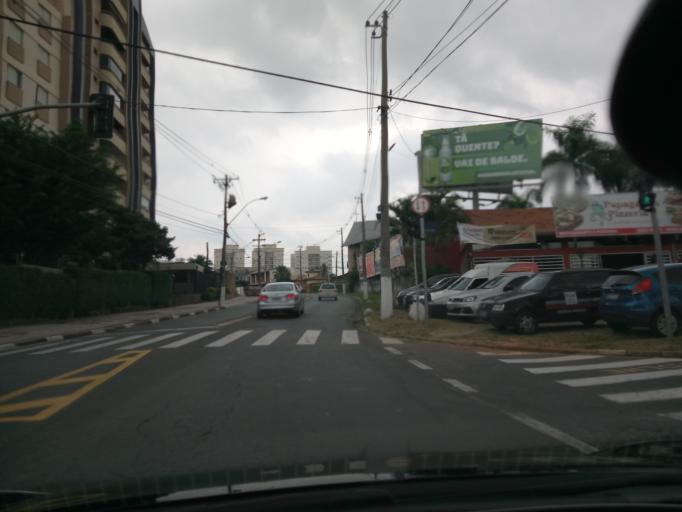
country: BR
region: Sao Paulo
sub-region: Campinas
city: Campinas
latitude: -22.8899
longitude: -47.0334
